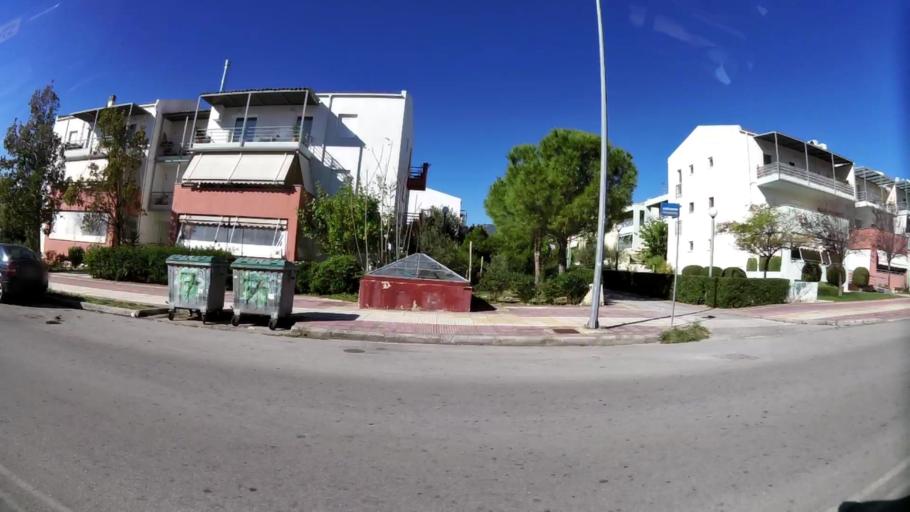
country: GR
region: Attica
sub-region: Nomarchia Anatolikis Attikis
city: Thrakomakedones
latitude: 38.1130
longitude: 23.7707
